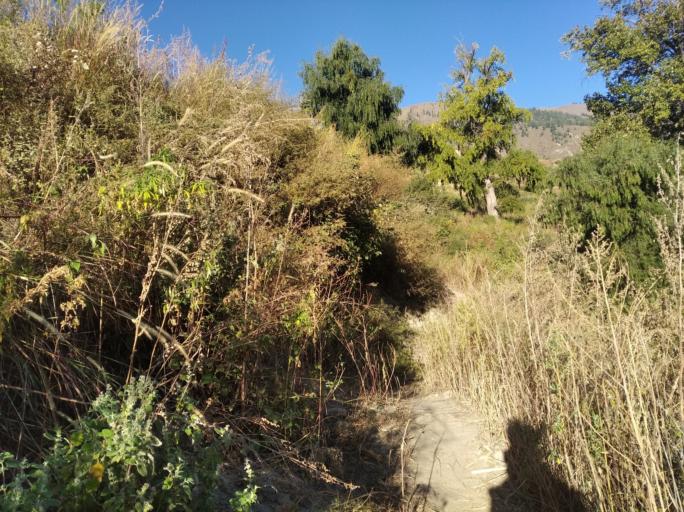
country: NP
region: Western Region
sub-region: Dhawalagiri Zone
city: Jomsom
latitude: 28.8806
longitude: 82.9829
